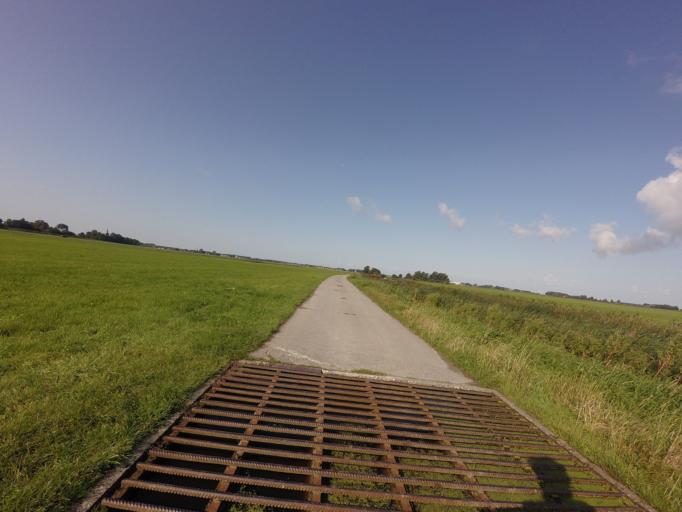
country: NL
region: Friesland
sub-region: Gemeente Franekeradeel
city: Franeker
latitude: 53.2035
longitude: 5.5763
